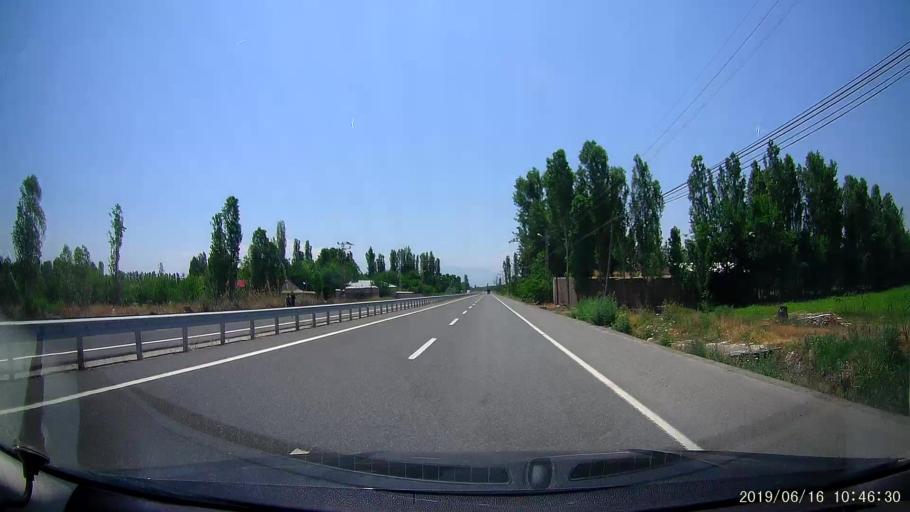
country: AM
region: Armavir
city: Shenavan
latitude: 40.0212
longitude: 43.8796
